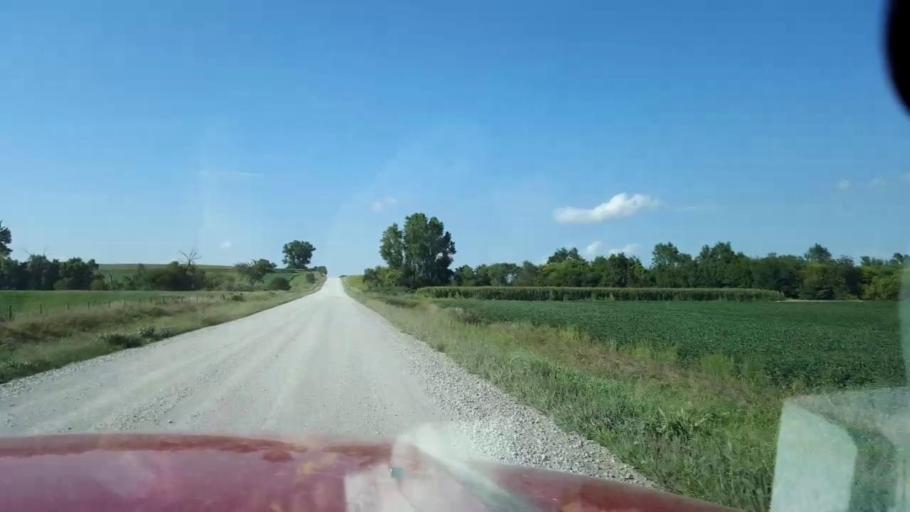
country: US
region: Iowa
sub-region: Pottawattamie County
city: Oakland
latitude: 41.2521
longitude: -95.5370
